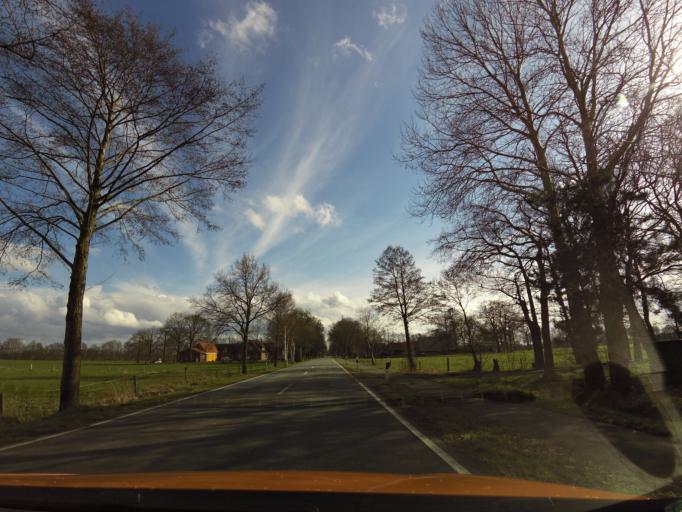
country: DE
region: Lower Saxony
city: Oldenburg
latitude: 53.0879
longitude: 8.2902
